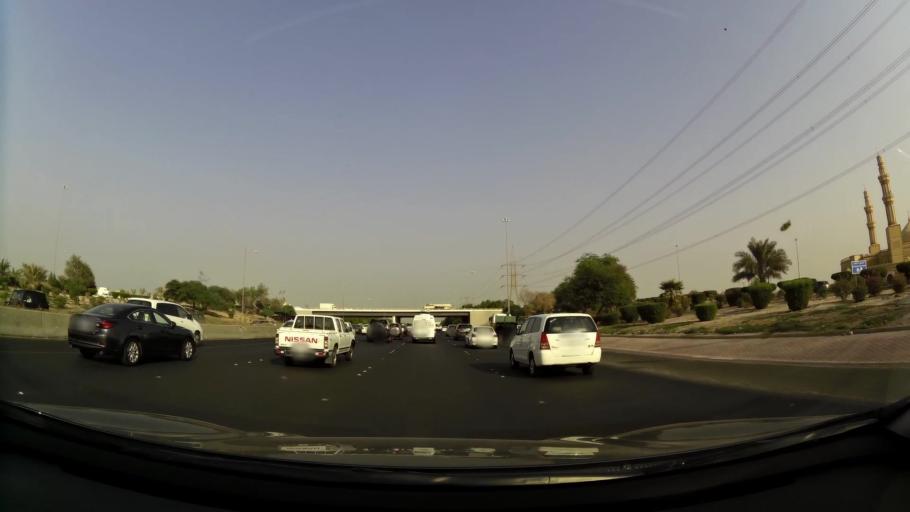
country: KW
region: Al Farwaniyah
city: Janub as Surrah
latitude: 29.3051
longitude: 47.9978
